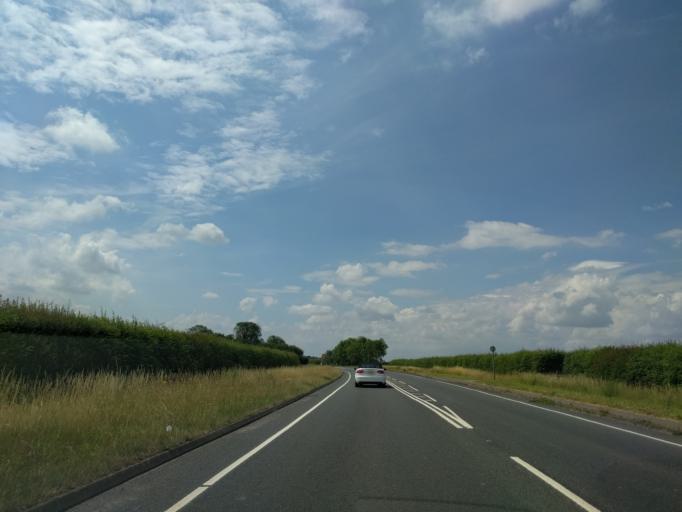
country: GB
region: England
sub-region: Cambridgeshire
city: Fulbourn
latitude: 52.2087
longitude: 0.1888
